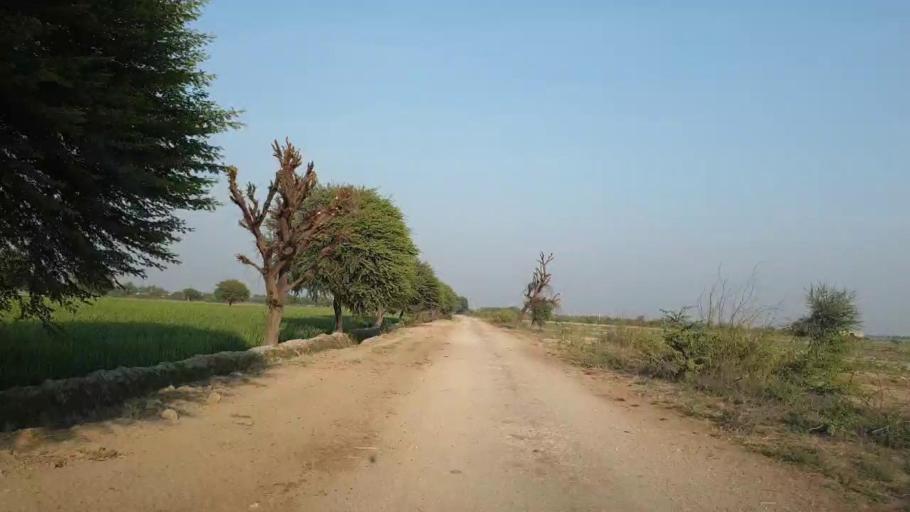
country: PK
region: Sindh
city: Mirpur Khas
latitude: 25.6719
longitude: 69.1955
